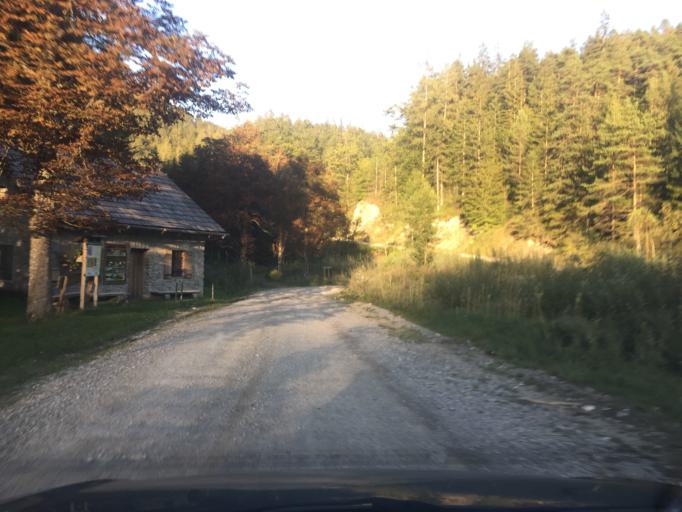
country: SI
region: Ravne na Koroskem
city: Kotlje
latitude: 46.4696
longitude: 14.9857
